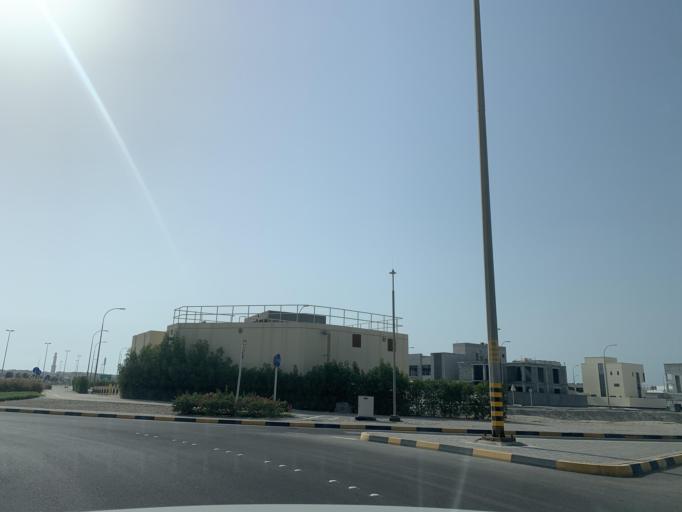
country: BH
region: Muharraq
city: Al Muharraq
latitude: 26.3086
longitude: 50.6352
